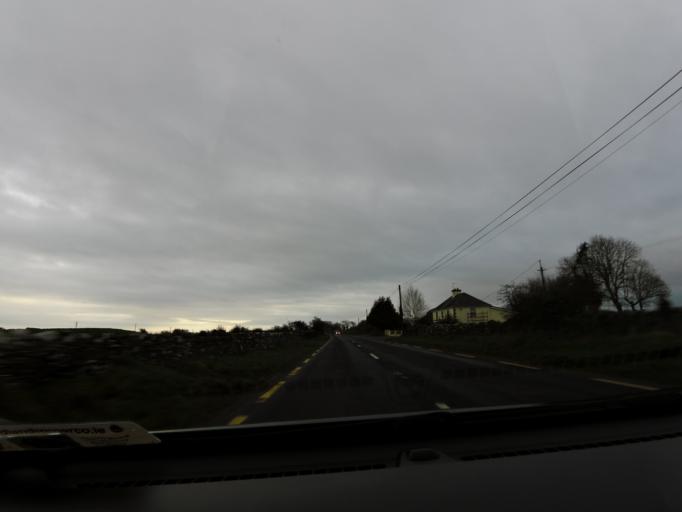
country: IE
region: Connaught
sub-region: County Galway
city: Loughrea
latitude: 53.1990
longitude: -8.4261
